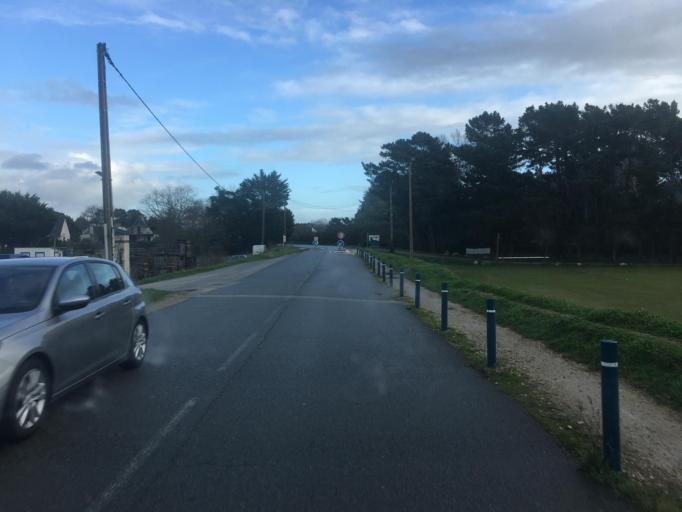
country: FR
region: Brittany
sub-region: Departement du Morbihan
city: Surzur
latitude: 47.5194
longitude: -2.6623
